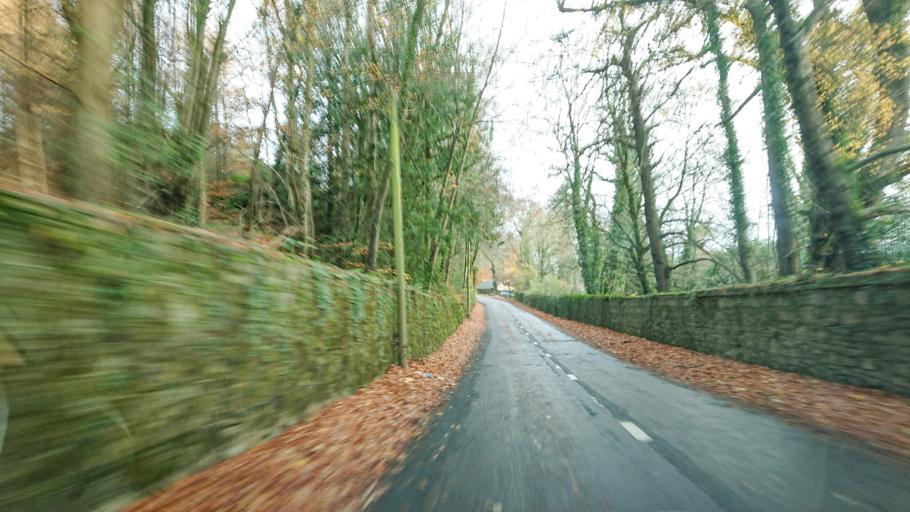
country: IE
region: Munster
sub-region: South Tipperary
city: Cluain Meala
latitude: 52.3562
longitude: -7.6080
